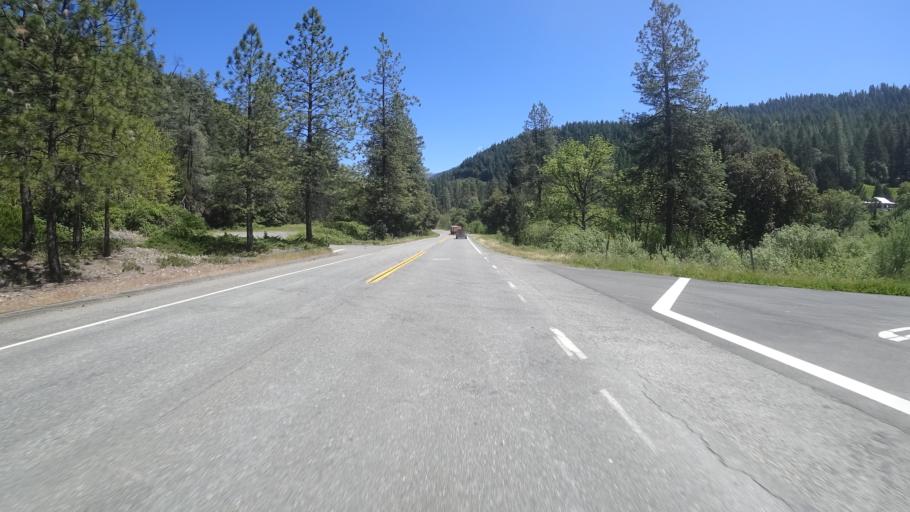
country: US
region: California
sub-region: Trinity County
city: Hayfork
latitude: 40.7398
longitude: -123.2520
